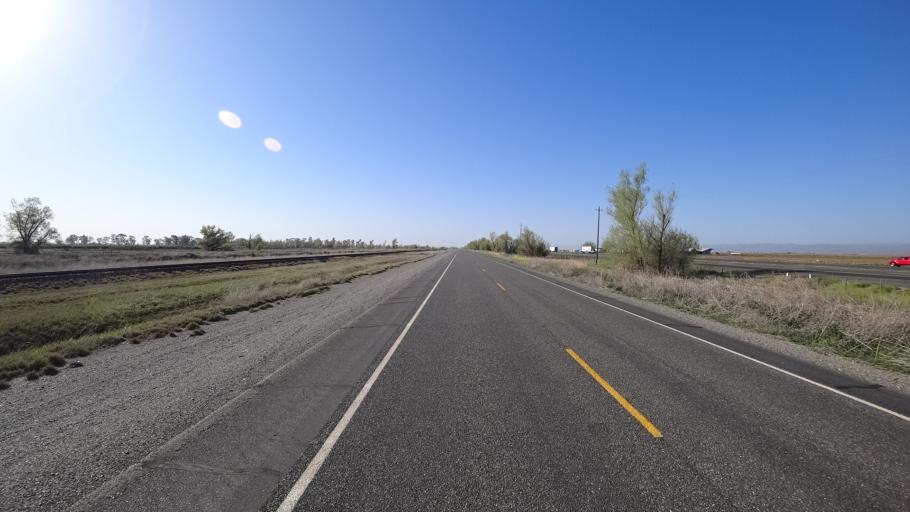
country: US
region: California
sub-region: Glenn County
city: Willows
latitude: 39.4390
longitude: -122.1928
